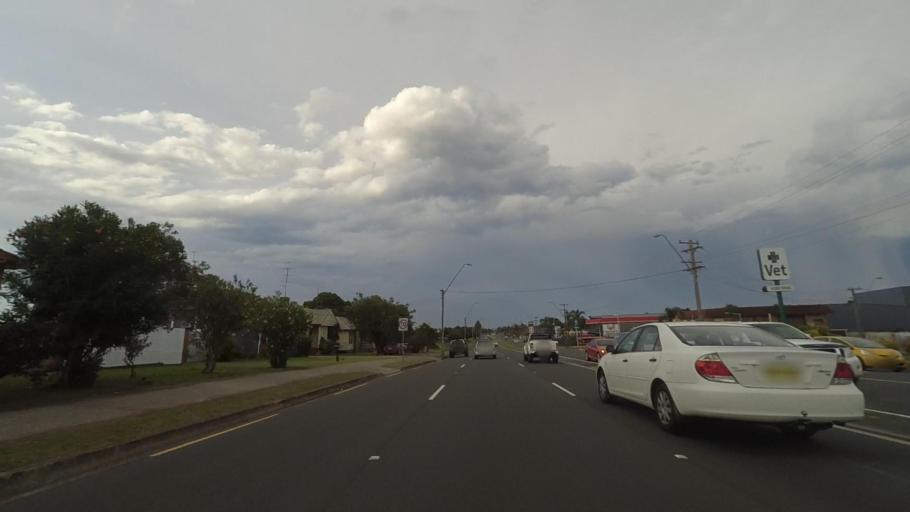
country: AU
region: New South Wales
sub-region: Shellharbour
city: Lake Illawarra
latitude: -34.5462
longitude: 150.8619
